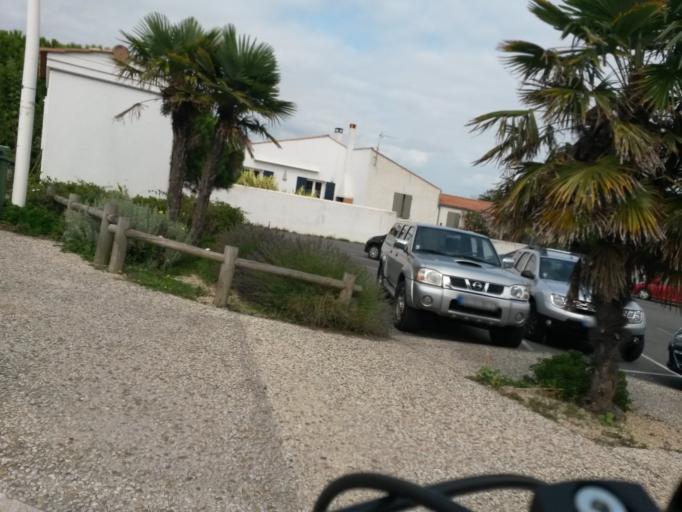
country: FR
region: Poitou-Charentes
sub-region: Departement de la Charente-Maritime
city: Saint-Trojan-les-Bains
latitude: 45.8427
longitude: -1.2067
